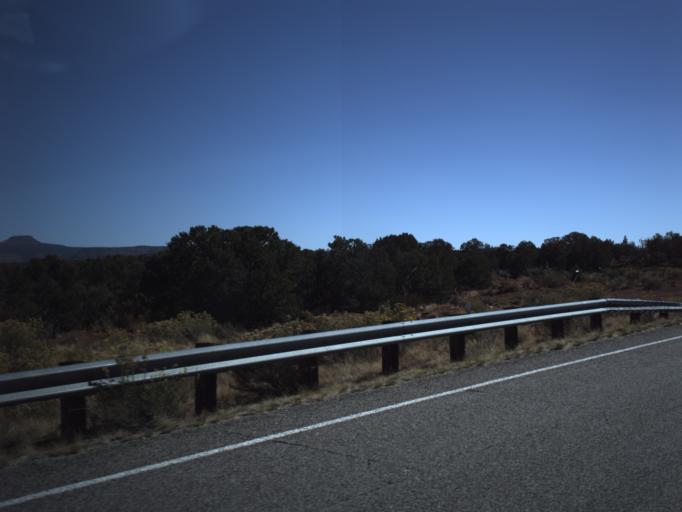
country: US
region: Utah
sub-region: San Juan County
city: Blanding
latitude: 37.5936
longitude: -110.0436
